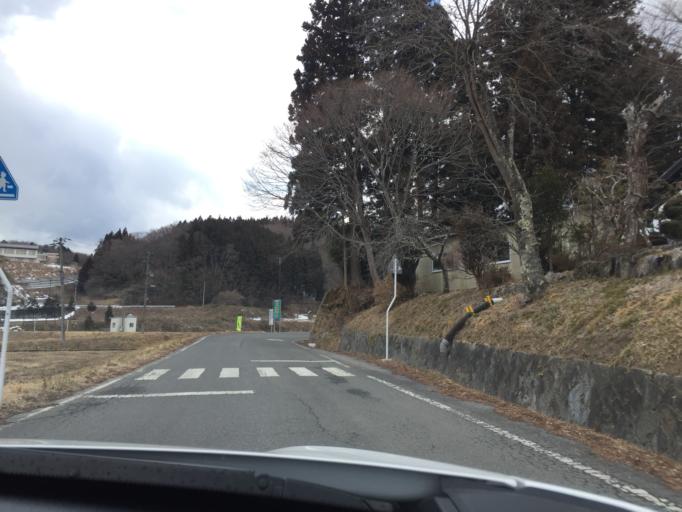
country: JP
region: Fukushima
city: Iwaki
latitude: 37.2450
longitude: 140.7267
